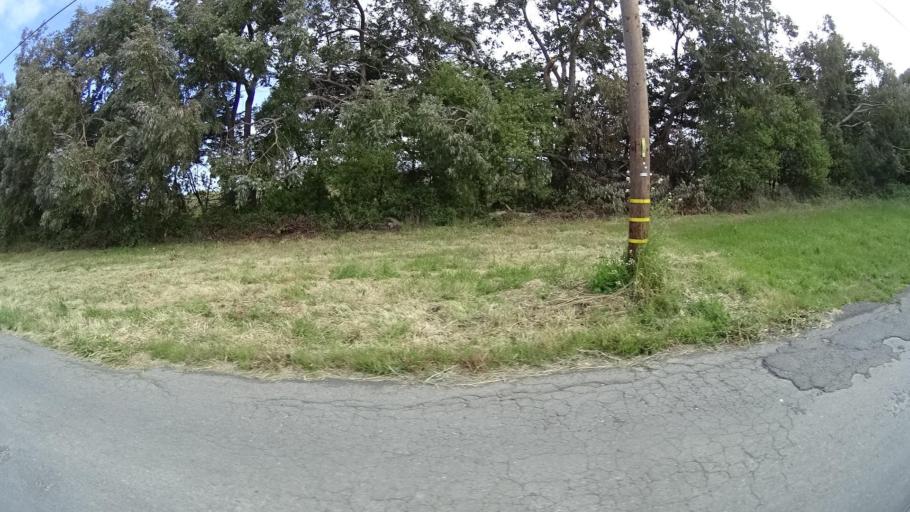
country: US
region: California
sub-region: Humboldt County
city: Arcata
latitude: 40.8816
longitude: -124.1025
